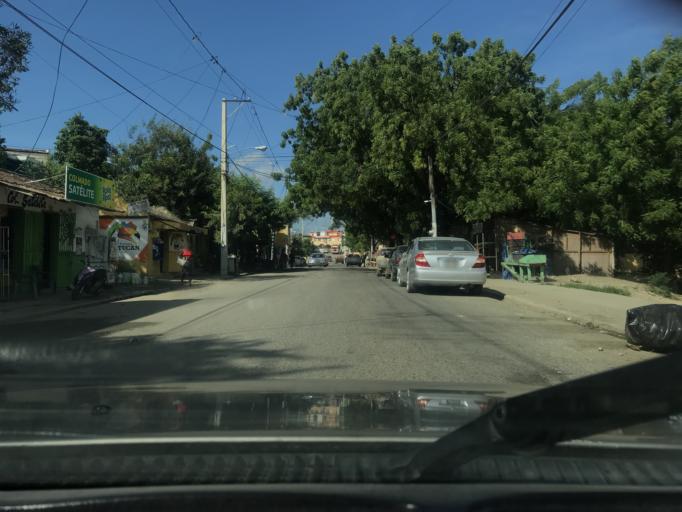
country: DO
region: Santiago
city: Palmar Arriba
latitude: 19.4832
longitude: -70.7498
